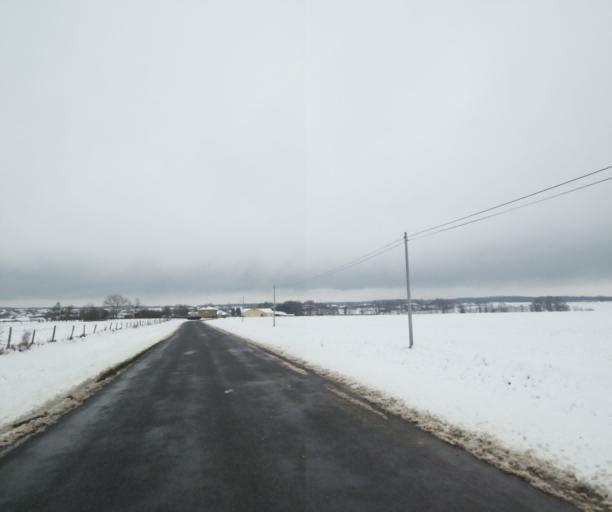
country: FR
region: Champagne-Ardenne
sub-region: Departement de la Haute-Marne
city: Laneuville-a-Remy
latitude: 48.4986
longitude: 4.8684
